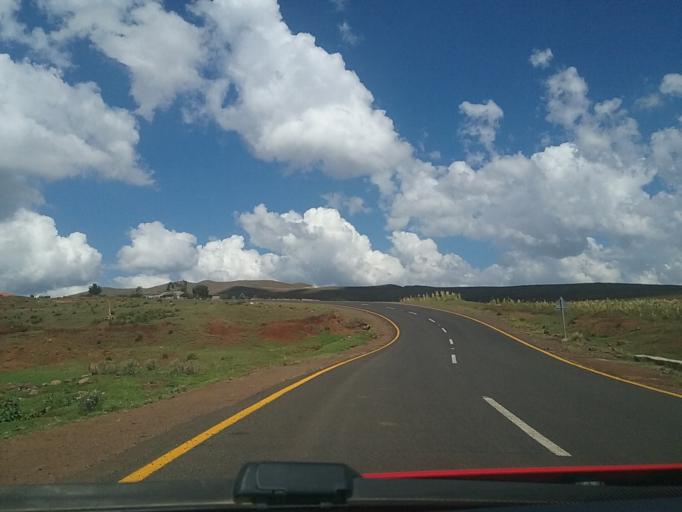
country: LS
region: Berea
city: Teyateyaneng
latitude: -29.2210
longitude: 27.8576
